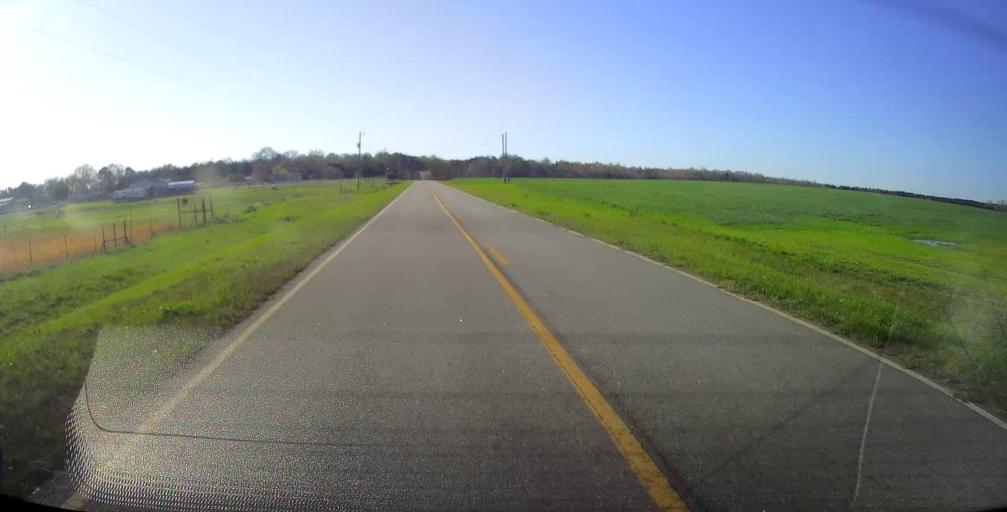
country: US
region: Georgia
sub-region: Dooly County
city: Unadilla
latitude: 32.3568
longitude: -83.6390
